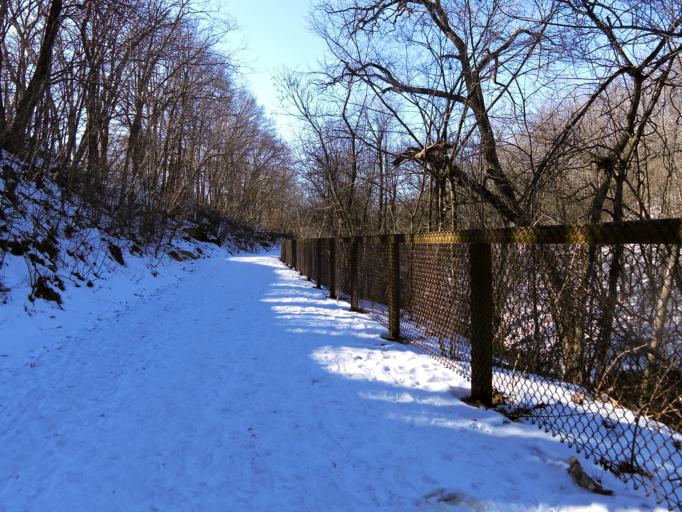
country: US
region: Minnesota
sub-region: Washington County
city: Stillwater
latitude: 45.0754
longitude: -92.8242
